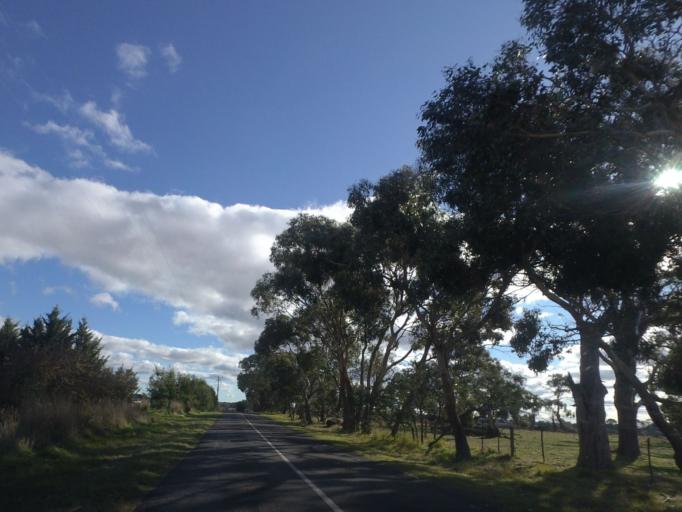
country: AU
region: Victoria
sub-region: Mount Alexander
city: Castlemaine
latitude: -37.2526
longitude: 144.4125
